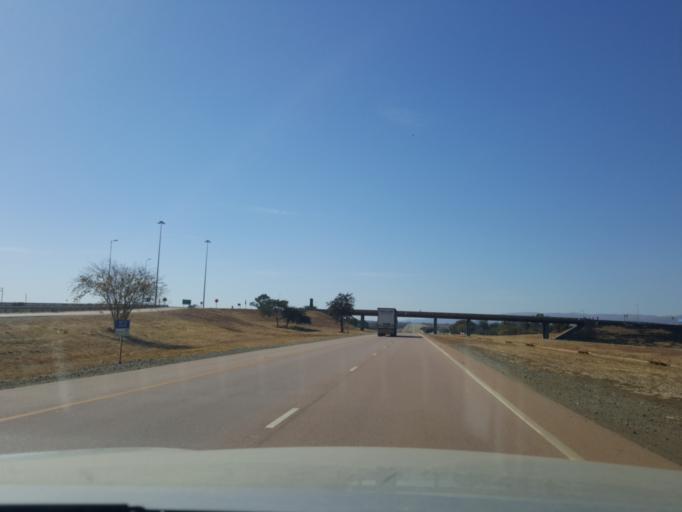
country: ZA
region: North-West
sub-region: Bojanala Platinum District Municipality
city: Brits
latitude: -25.7373
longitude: 27.5536
